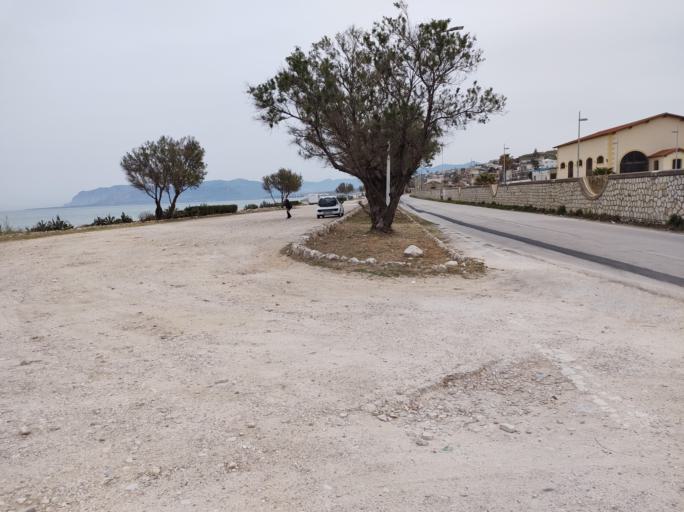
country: IT
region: Sicily
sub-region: Trapani
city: Castellammare del Golfo
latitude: 38.0249
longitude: 12.9126
